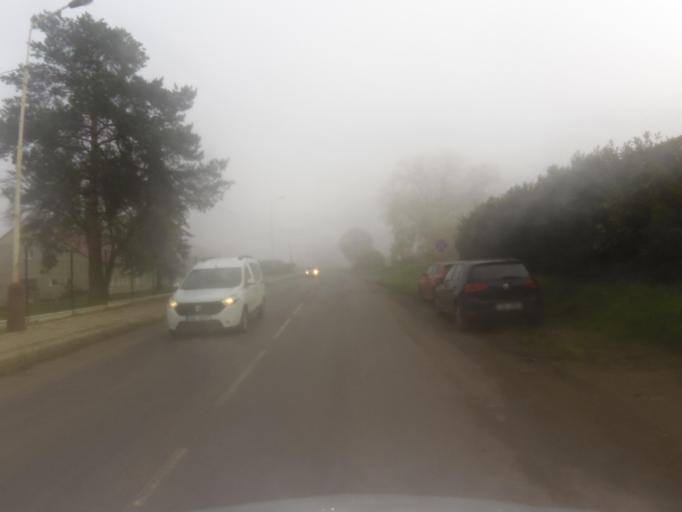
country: CZ
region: Ustecky
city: Zatec
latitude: 50.3250
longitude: 13.5600
